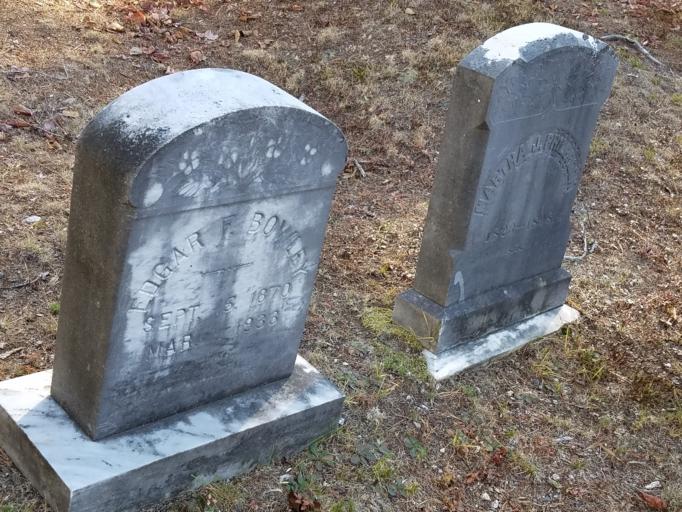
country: US
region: New Hampshire
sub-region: Carroll County
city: Effingham
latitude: 43.6743
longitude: -71.0211
